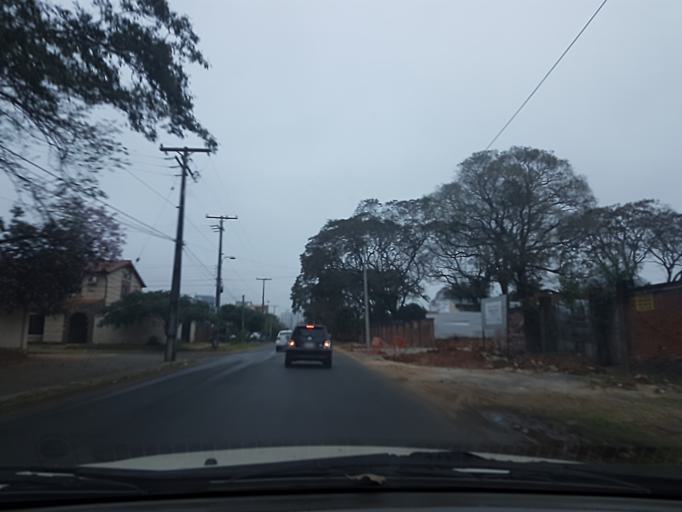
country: PY
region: Central
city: Fernando de la Mora
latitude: -25.2731
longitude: -57.5589
